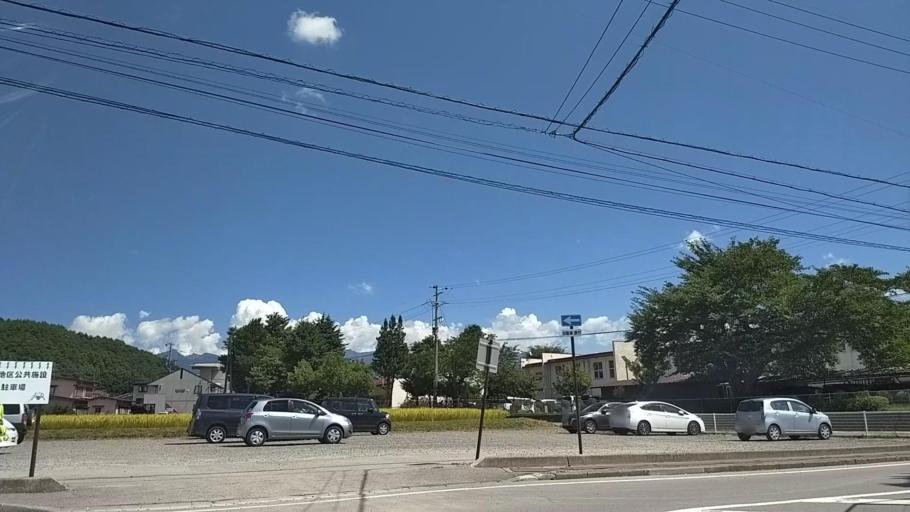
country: JP
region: Nagano
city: Chino
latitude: 35.9988
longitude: 138.1534
